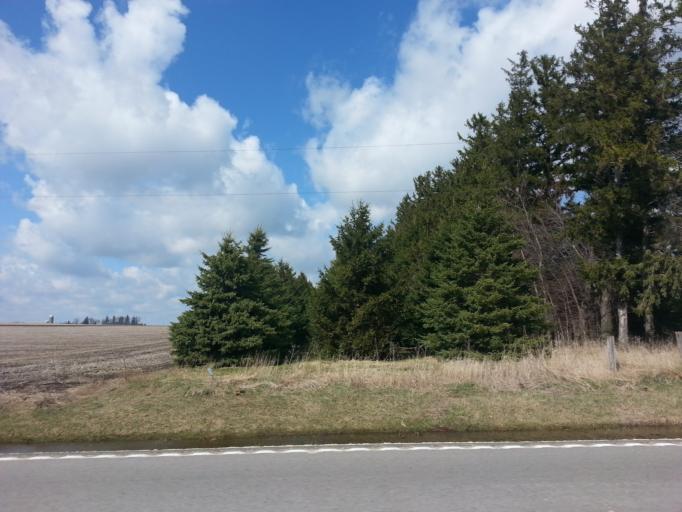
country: US
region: Minnesota
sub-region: Dodge County
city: Dodge Center
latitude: 44.0879
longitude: -92.8636
